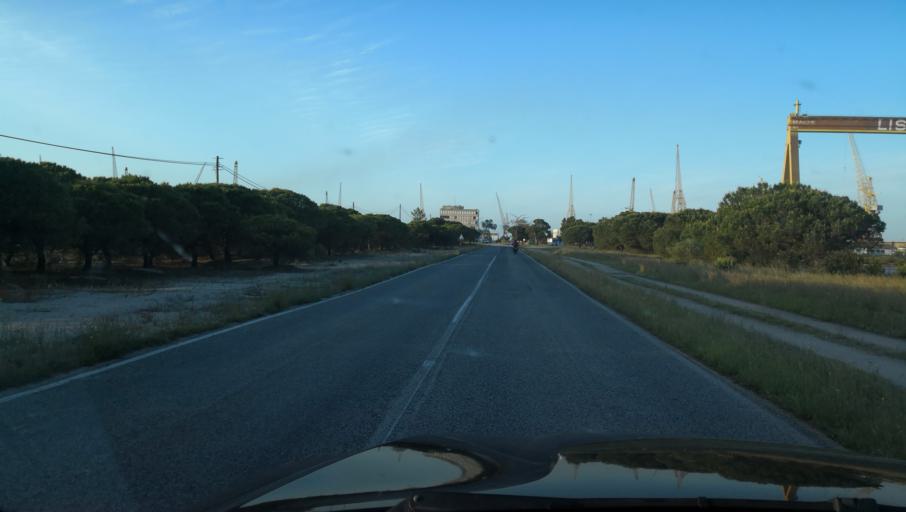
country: PT
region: Setubal
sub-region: Setubal
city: Setubal
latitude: 38.4849
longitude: -8.7932
